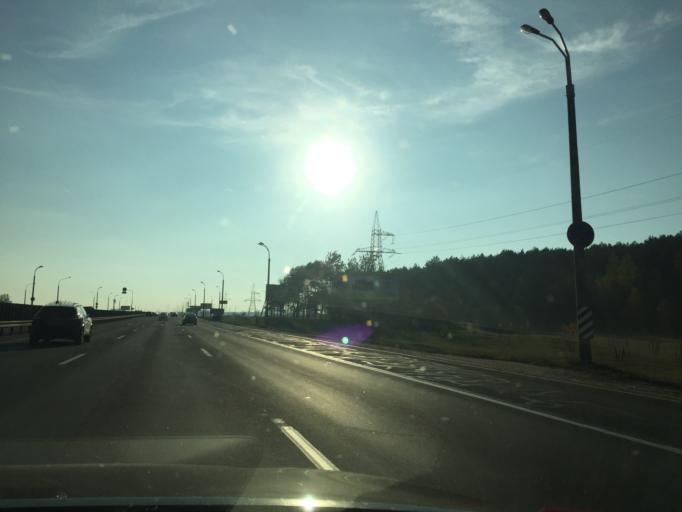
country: BY
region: Minsk
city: Zhdanovichy
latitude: 53.9541
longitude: 27.4498
